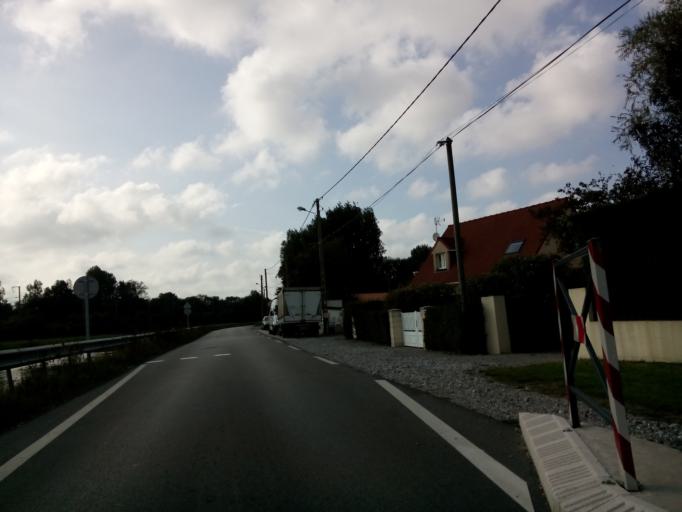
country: FR
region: Nord-Pas-de-Calais
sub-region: Departement du Pas-de-Calais
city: Coulogne
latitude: 50.9216
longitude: 1.8780
